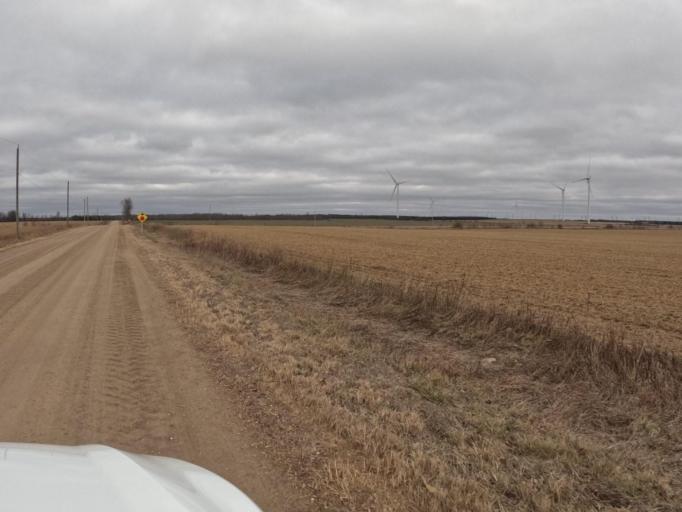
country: CA
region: Ontario
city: Shelburne
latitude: 43.8833
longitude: -80.3815
